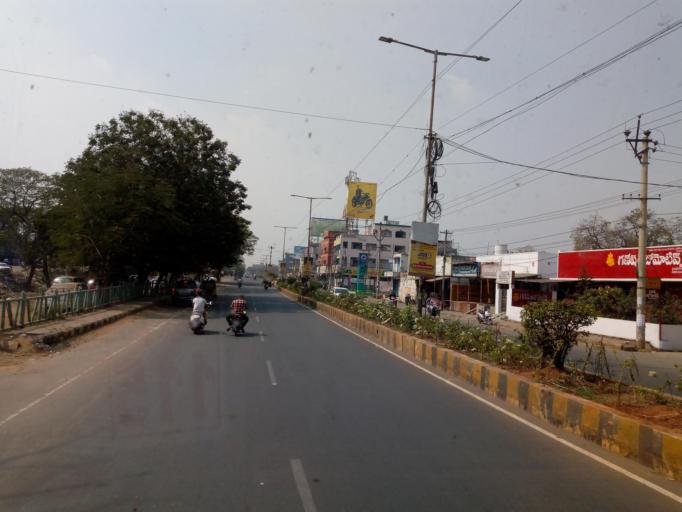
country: IN
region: Andhra Pradesh
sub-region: West Godavari
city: Eluru
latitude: 16.7097
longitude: 81.1059
